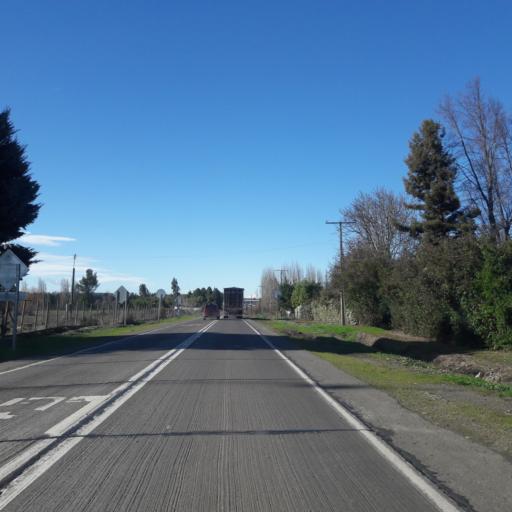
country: CL
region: Araucania
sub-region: Provincia de Malleco
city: Angol
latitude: -37.7744
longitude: -72.5454
